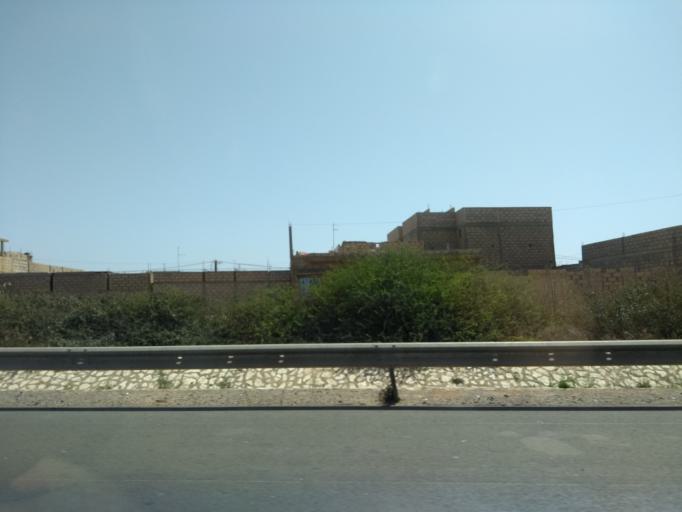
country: SN
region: Dakar
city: Pikine
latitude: 14.7392
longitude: -17.2658
